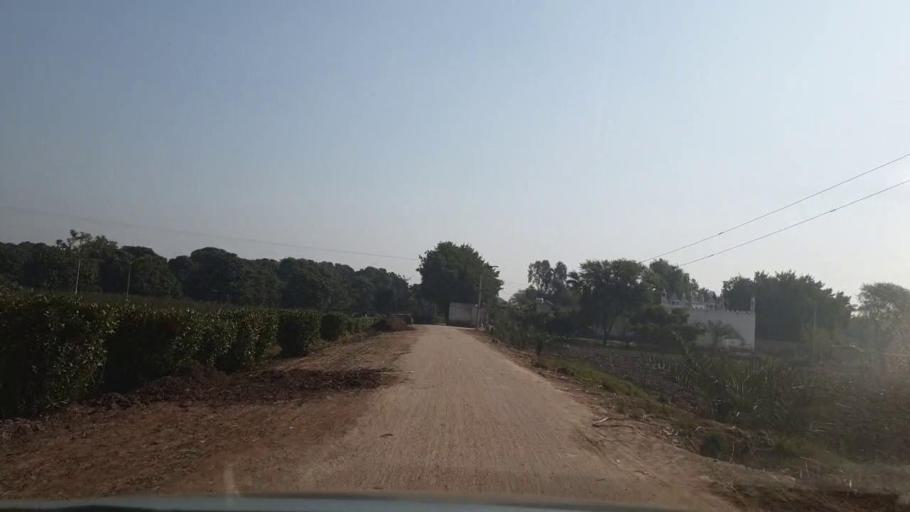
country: PK
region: Sindh
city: Matiari
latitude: 25.5589
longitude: 68.4919
